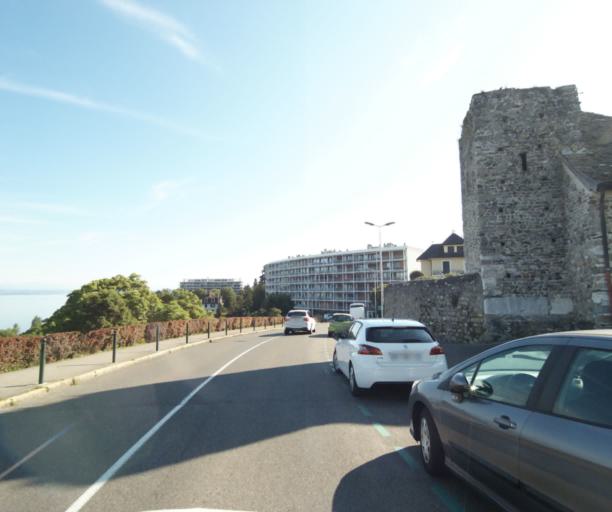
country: FR
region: Rhone-Alpes
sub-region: Departement de la Haute-Savoie
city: Thonon-les-Bains
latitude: 46.3750
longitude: 6.4814
